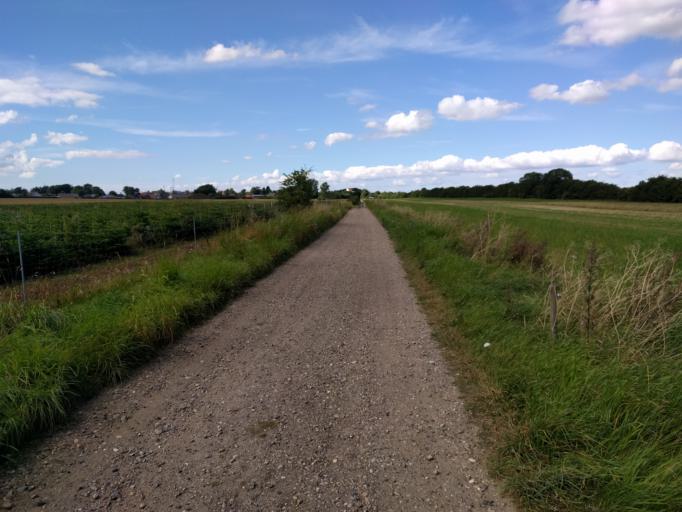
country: DK
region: Central Jutland
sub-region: Viborg Kommune
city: Bjerringbro
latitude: 56.5253
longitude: 9.5852
